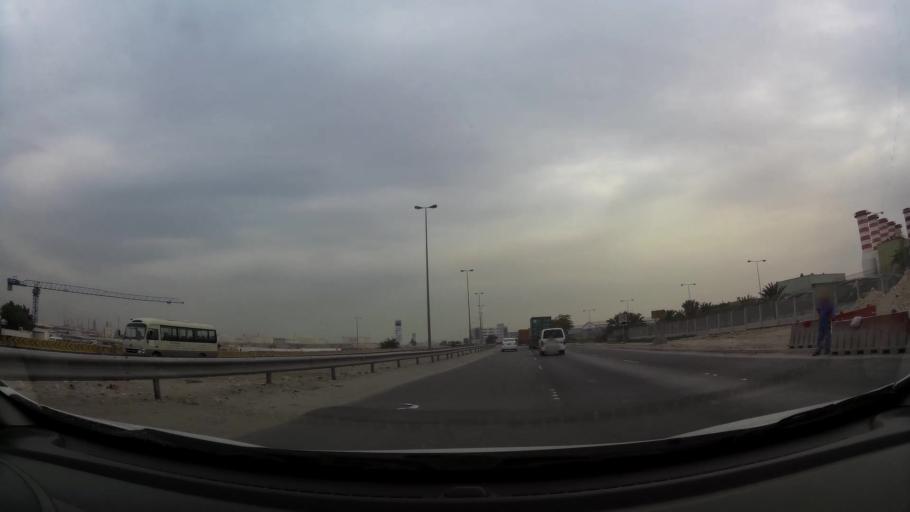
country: BH
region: Northern
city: Ar Rifa'
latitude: 26.1221
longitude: 50.5916
